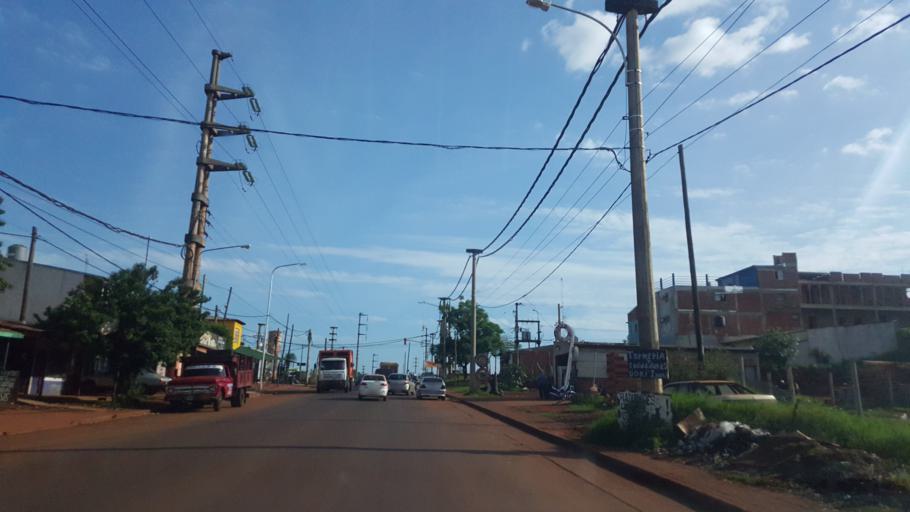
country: AR
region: Misiones
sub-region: Departamento de Capital
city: Posadas
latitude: -27.4267
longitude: -55.9142
